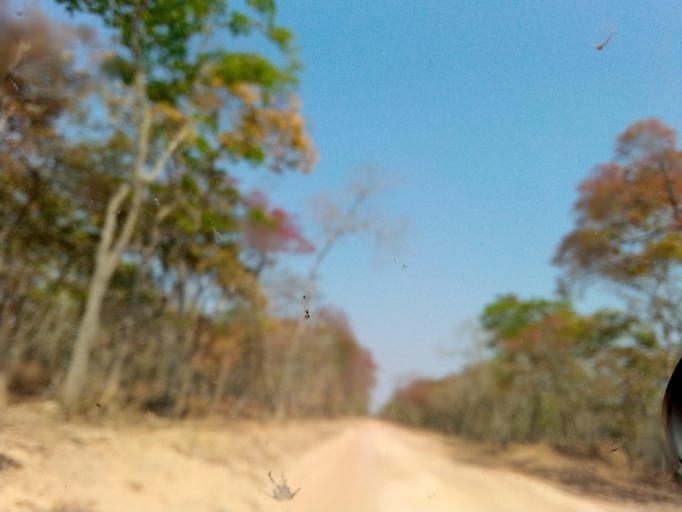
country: ZM
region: Northern
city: Mpika
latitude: -12.2422
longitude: 30.8328
